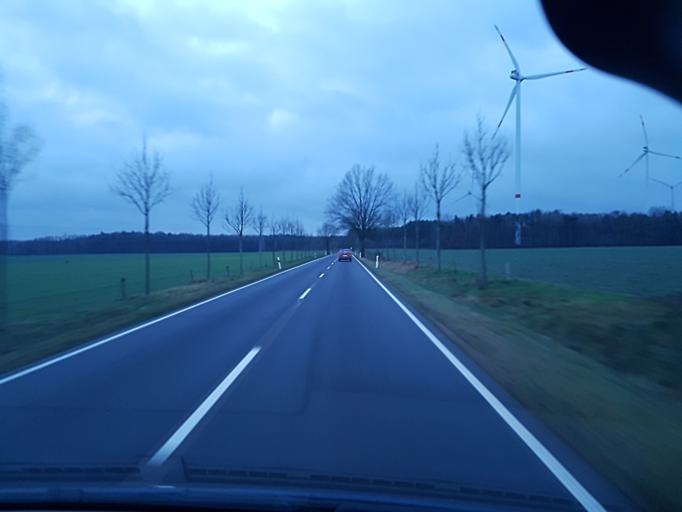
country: DE
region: Brandenburg
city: Sallgast
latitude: 51.6312
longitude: 13.8452
